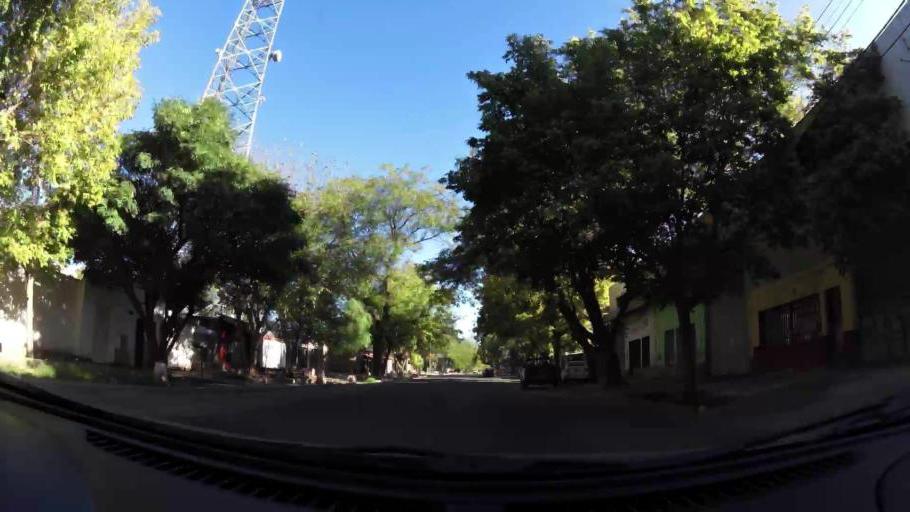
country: AR
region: Mendoza
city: Las Heras
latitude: -32.8566
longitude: -68.8272
